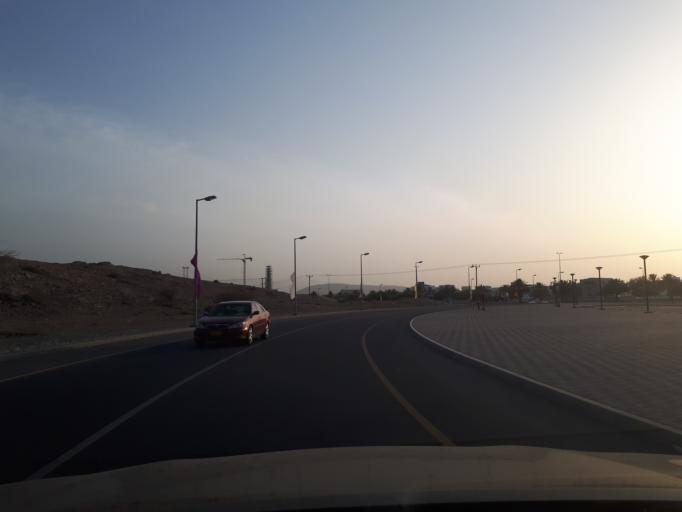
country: OM
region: Muhafazat Masqat
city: As Sib al Jadidah
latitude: 23.5844
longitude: 58.1993
